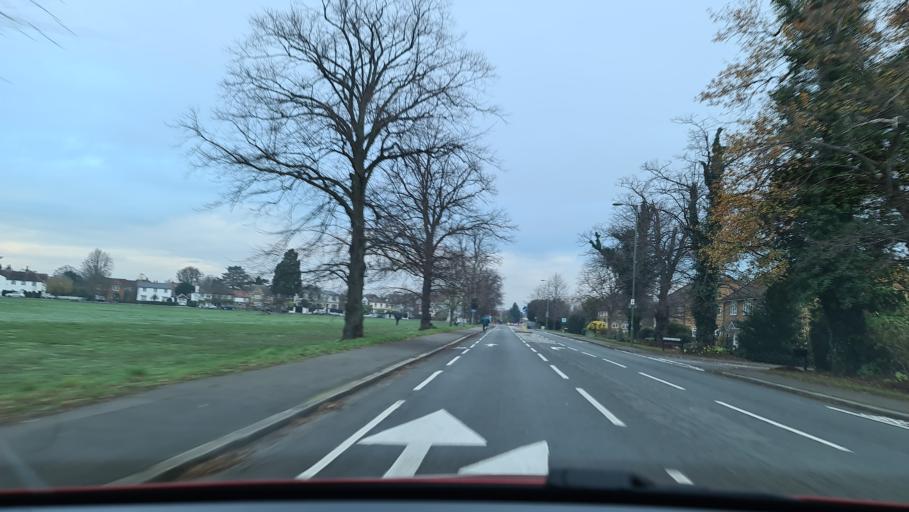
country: GB
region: England
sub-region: Surrey
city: Thames Ditton
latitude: 51.3848
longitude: -0.3324
